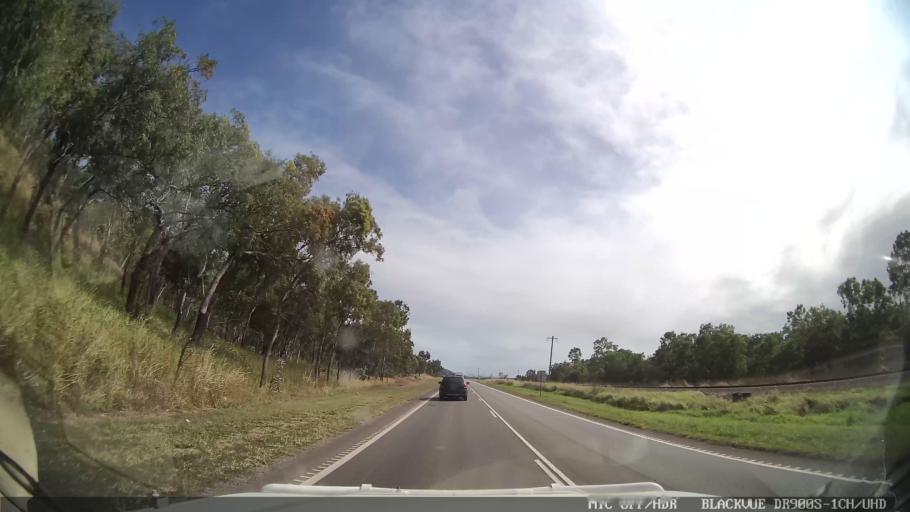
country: AU
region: Queensland
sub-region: Townsville
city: Townsville
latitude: -19.4010
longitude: 147.0250
